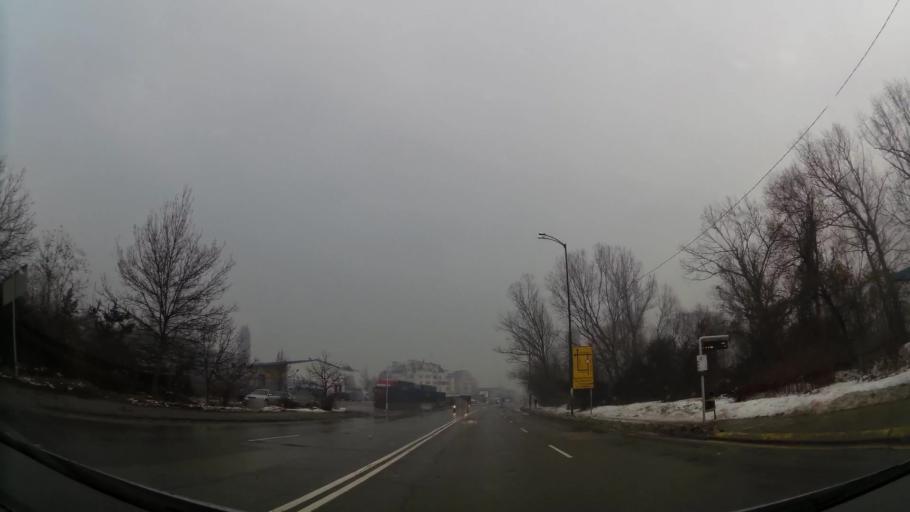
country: BG
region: Sofia-Capital
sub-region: Stolichna Obshtina
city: Sofia
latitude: 42.6882
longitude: 23.2631
